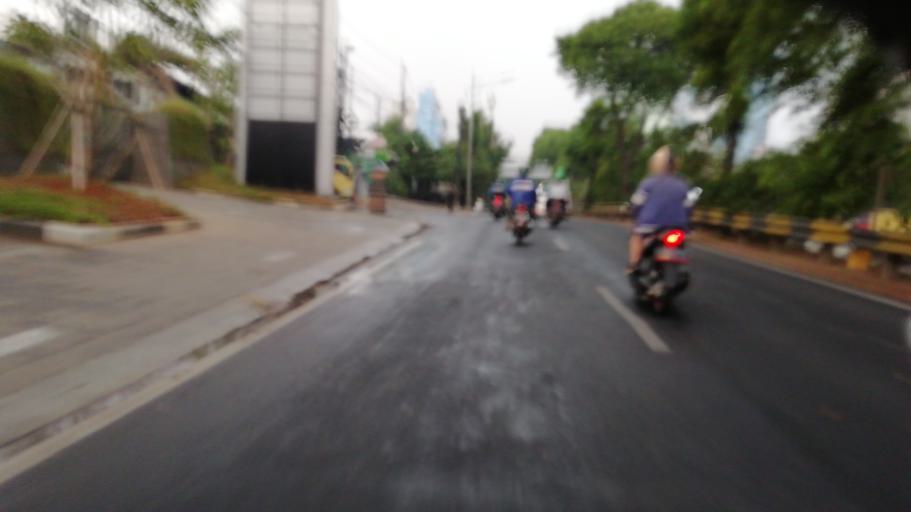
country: ID
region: Jakarta Raya
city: Jakarta
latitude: -6.2990
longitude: 106.8328
